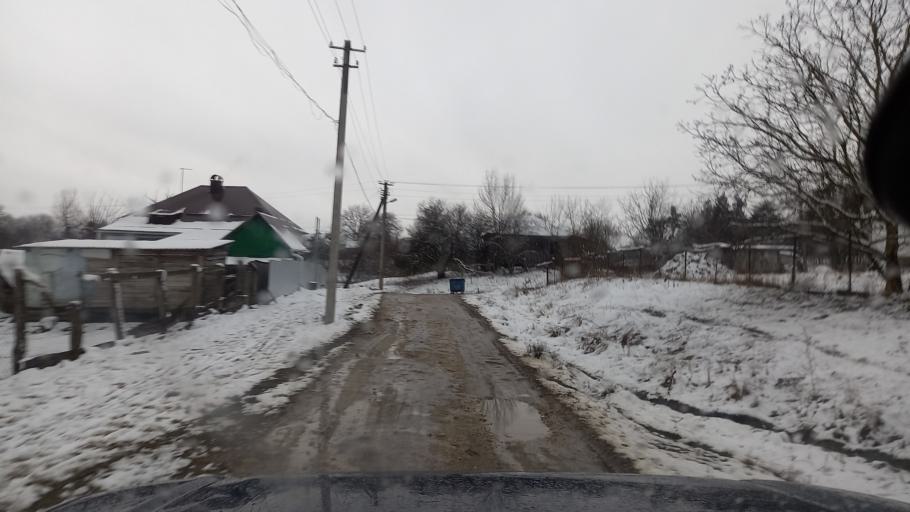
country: RU
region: Adygeya
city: Abadzekhskaya
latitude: 44.3546
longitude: 40.4137
